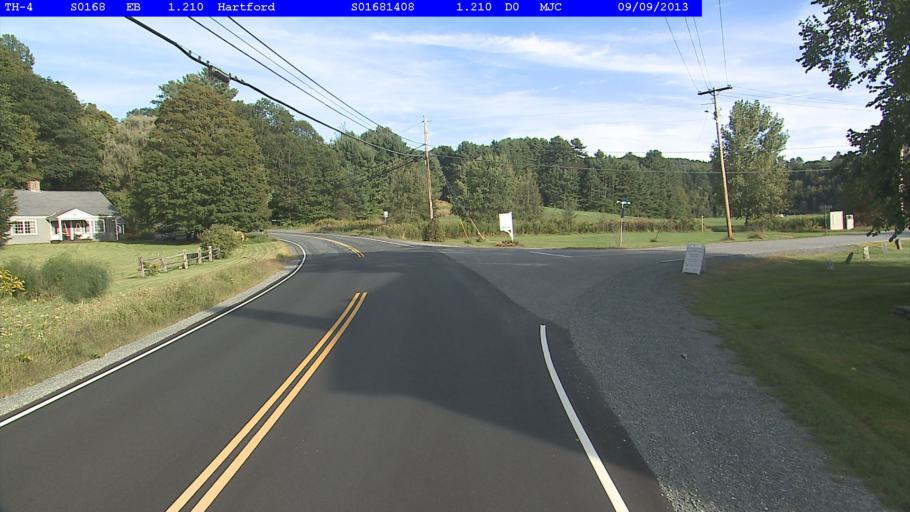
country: US
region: Vermont
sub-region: Windsor County
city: White River Junction
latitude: 43.6458
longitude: -72.4002
